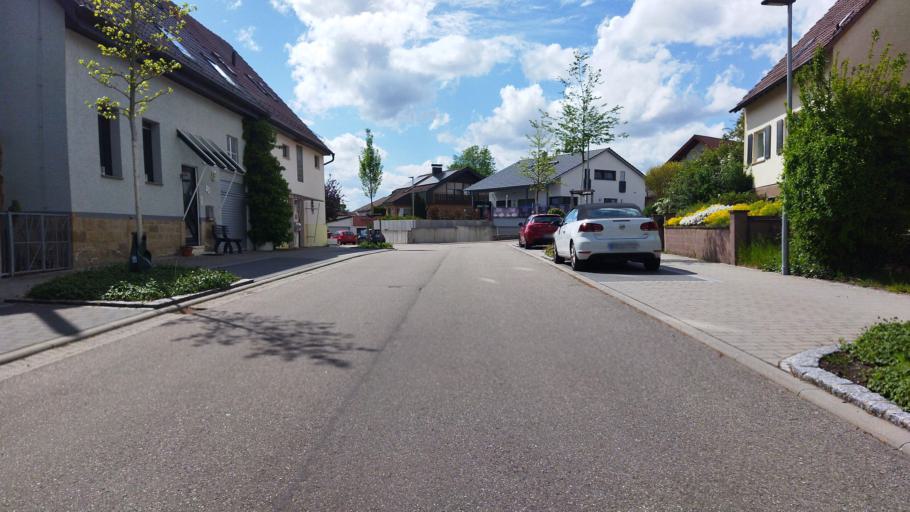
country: DE
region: Baden-Wuerttemberg
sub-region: Regierungsbezirk Stuttgart
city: Bad Rappenau
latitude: 49.2153
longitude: 9.0918
